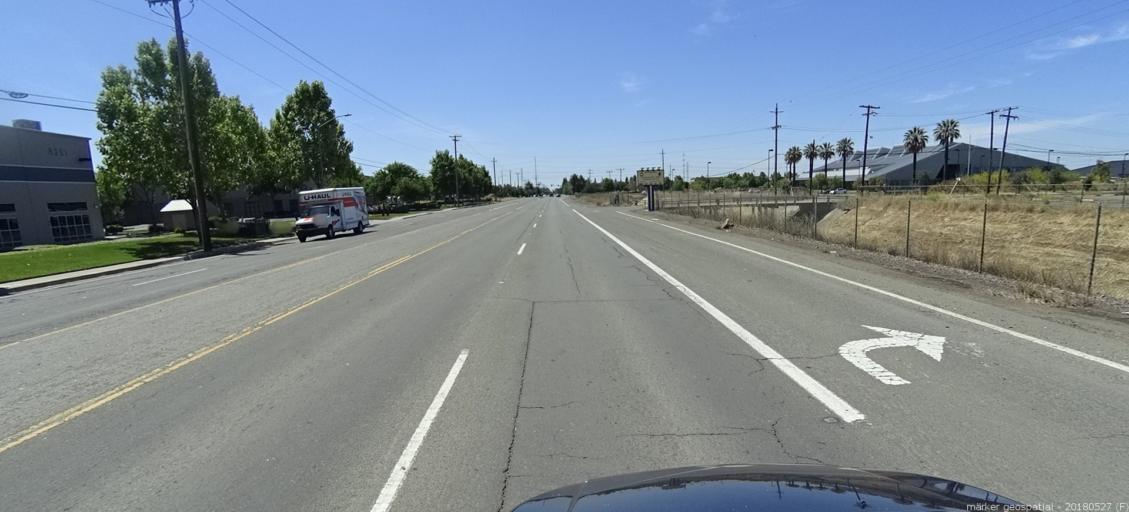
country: US
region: California
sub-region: Sacramento County
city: Florin
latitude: 38.5137
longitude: -121.3906
